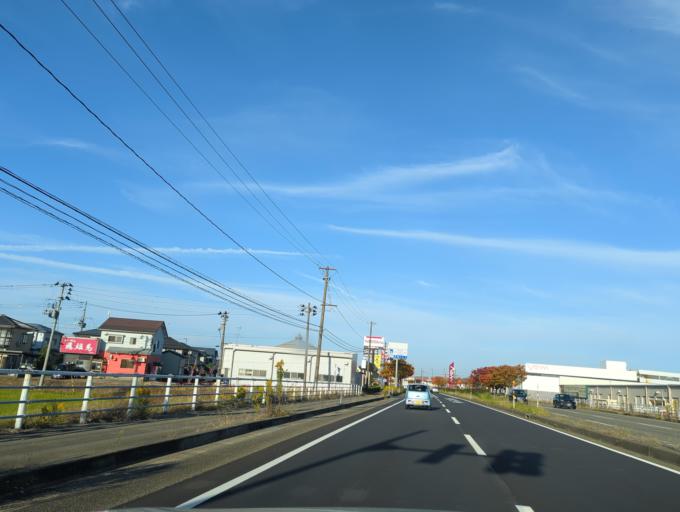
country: JP
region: Niigata
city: Mitsuke
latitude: 37.5397
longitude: 138.8874
